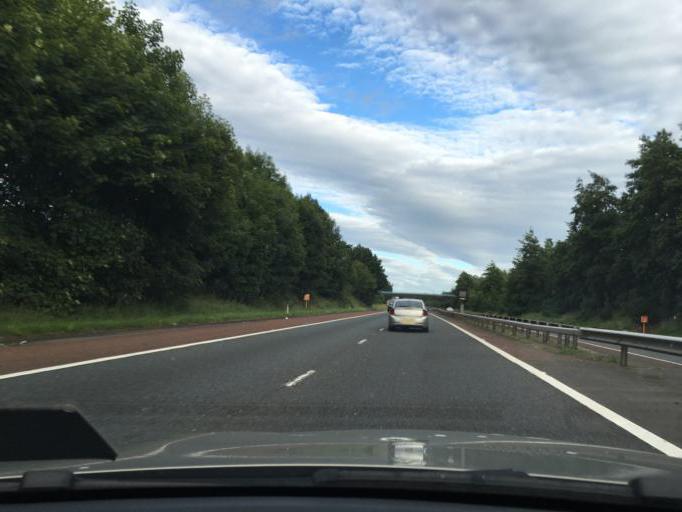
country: GB
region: Northern Ireland
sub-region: Antrim Borough
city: Templepatrick
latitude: 54.7051
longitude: -6.0547
